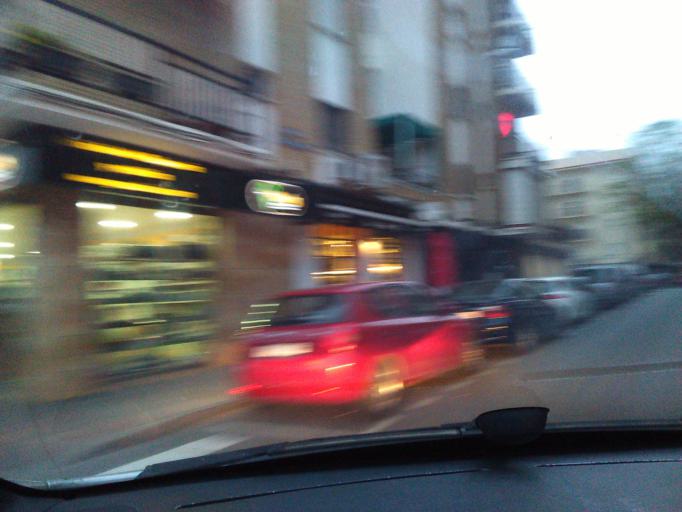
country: ES
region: Andalusia
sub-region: Provincia de Sevilla
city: Sevilla
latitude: 37.3745
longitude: -6.0041
